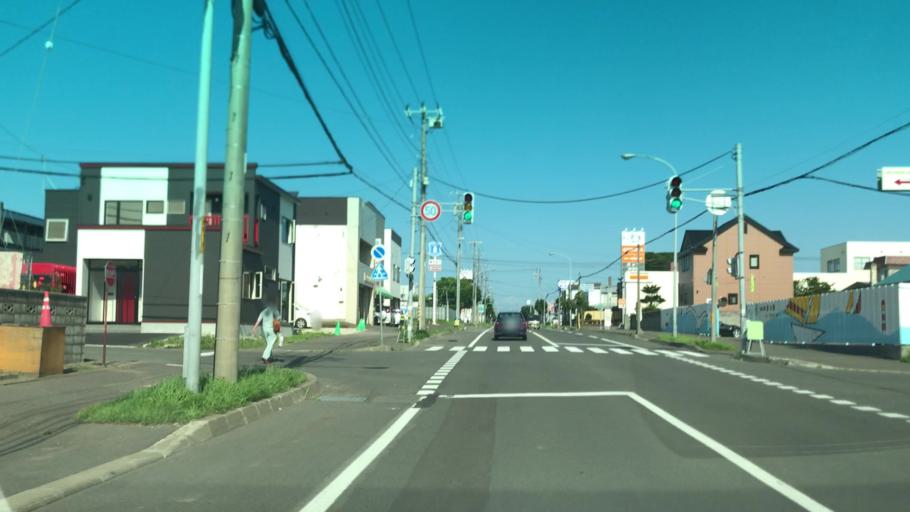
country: JP
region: Hokkaido
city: Iwanai
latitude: 42.9827
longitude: 140.5288
